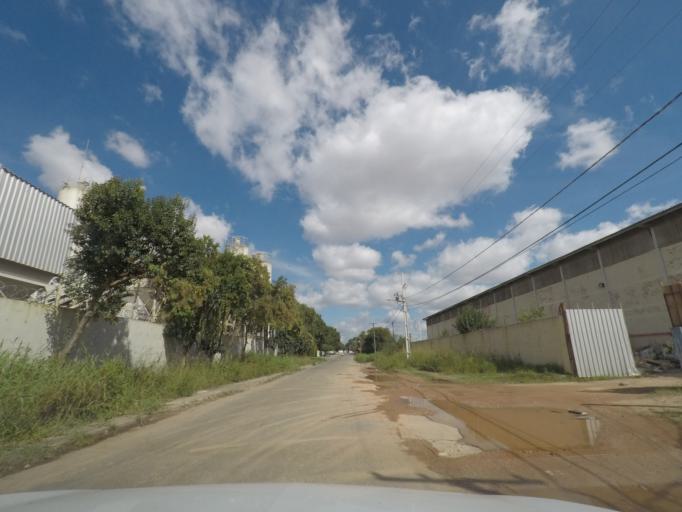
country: BR
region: Parana
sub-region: Sao Jose Dos Pinhais
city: Sao Jose dos Pinhais
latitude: -25.4939
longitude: -49.2304
